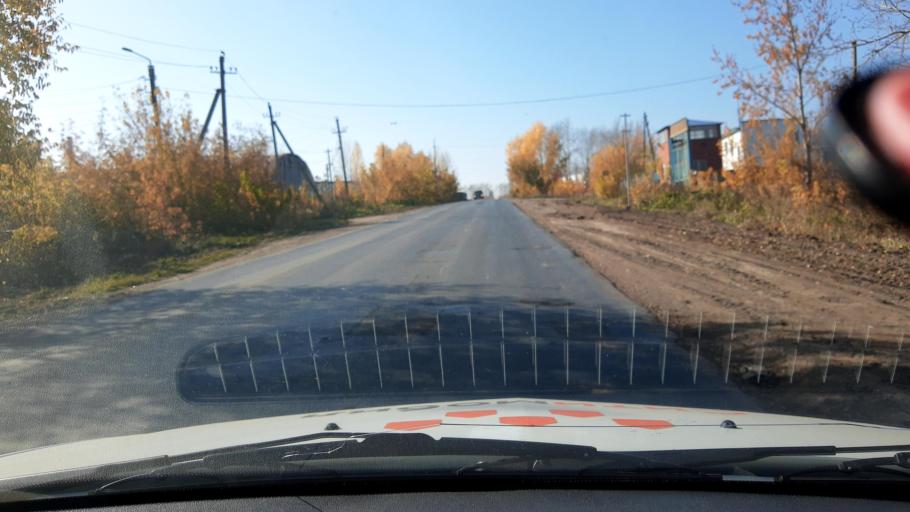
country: RU
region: Bashkortostan
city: Ufa
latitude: 54.8627
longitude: 56.1179
